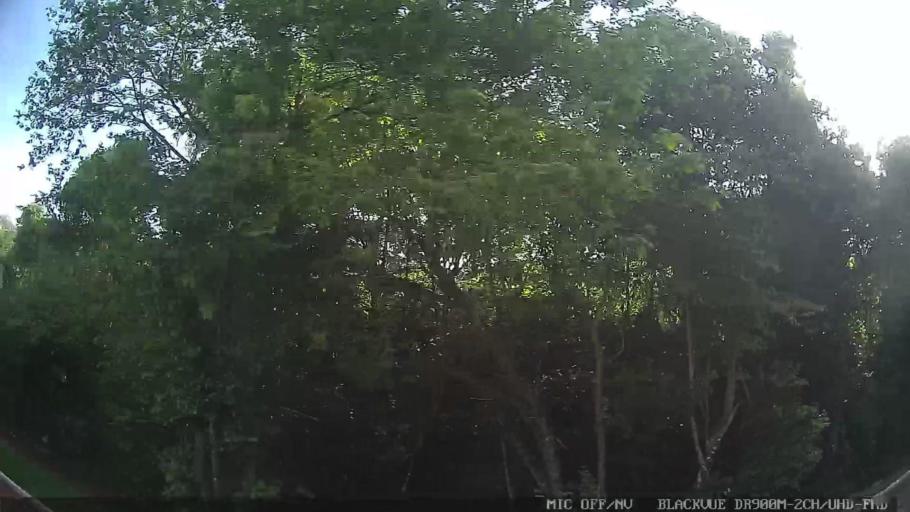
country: BR
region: Sao Paulo
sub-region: Serra Negra
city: Serra Negra
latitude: -22.6897
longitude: -46.6839
